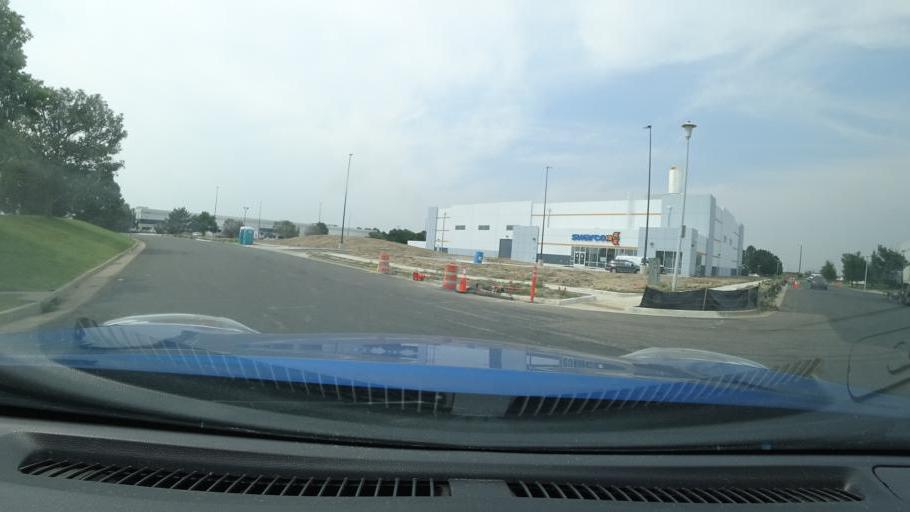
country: US
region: Colorado
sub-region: Adams County
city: Aurora
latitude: 39.7570
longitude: -104.7757
